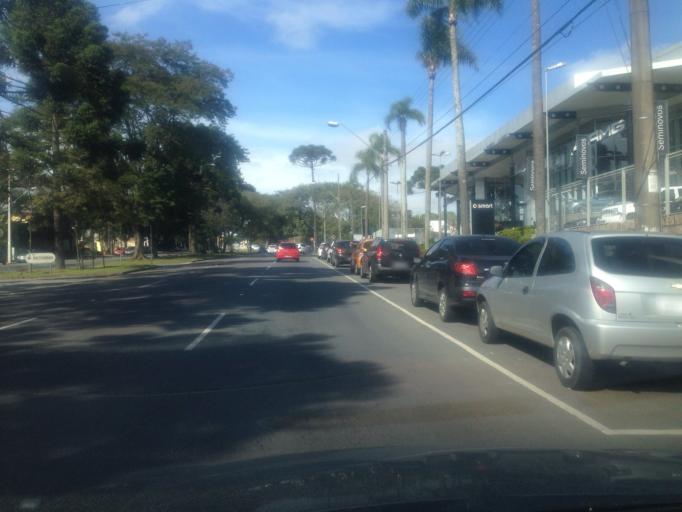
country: BR
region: Parana
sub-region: Curitiba
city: Curitiba
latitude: -25.4182
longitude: -49.2410
